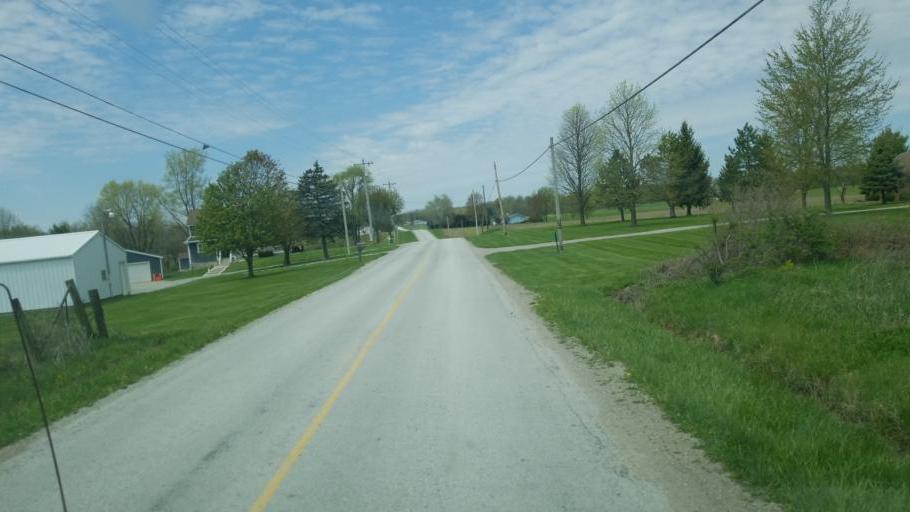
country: US
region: Ohio
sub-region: Hardin County
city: Ada
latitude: 40.7087
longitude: -83.7926
